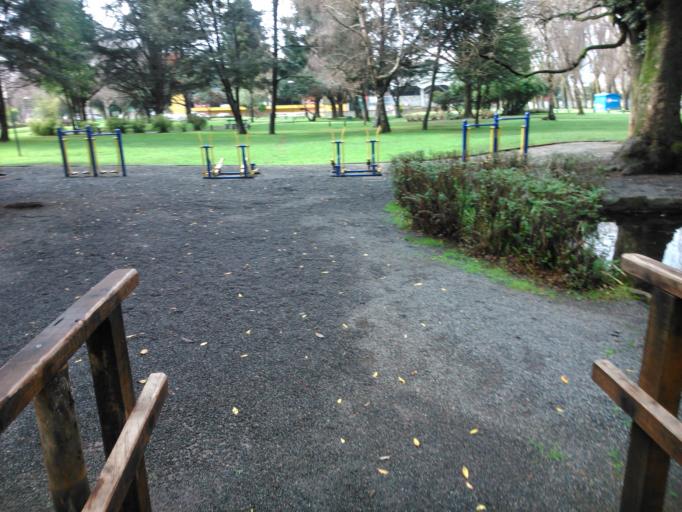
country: CL
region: Araucania
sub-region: Provincia de Cautin
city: Temuco
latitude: -38.7420
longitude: -72.6222
